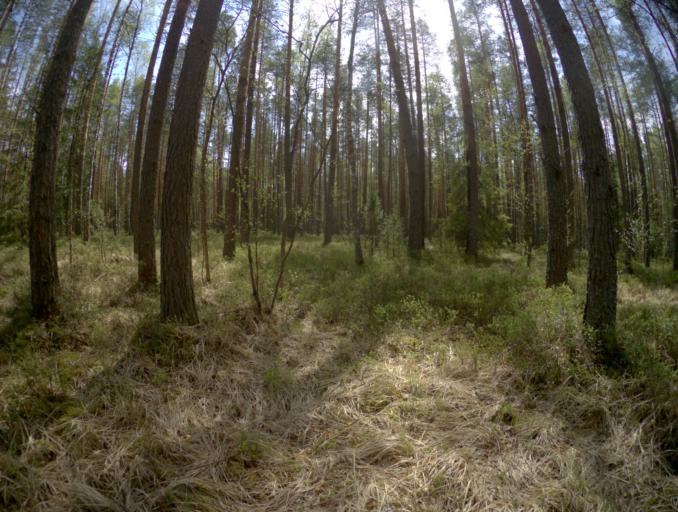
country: RU
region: Vladimir
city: Golovino
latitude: 55.9257
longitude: 40.3853
